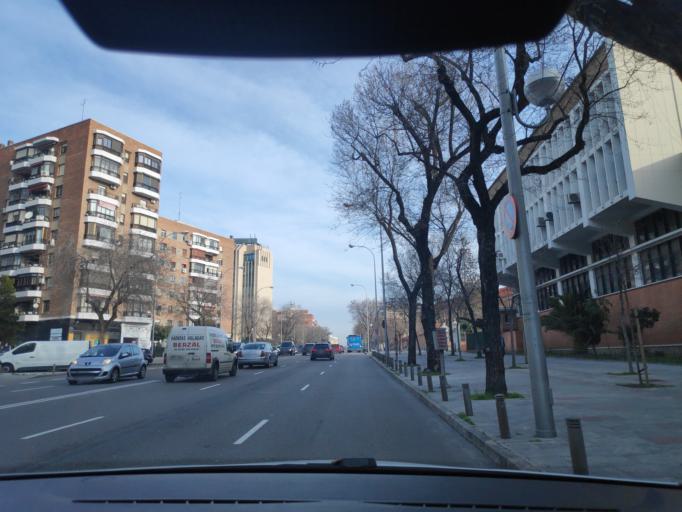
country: ES
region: Madrid
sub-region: Provincia de Madrid
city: Chamartin
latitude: 40.4530
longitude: -3.6773
